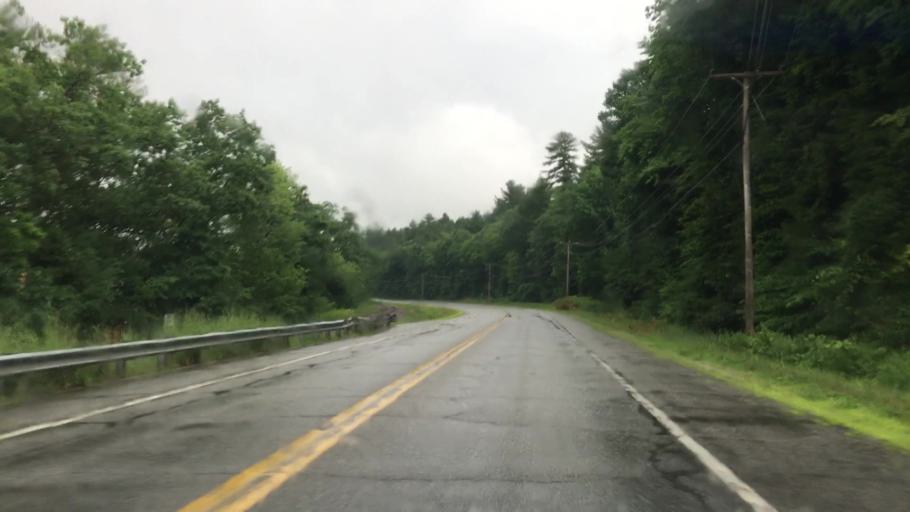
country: US
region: Maine
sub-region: Kennebec County
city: Pittston
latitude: 44.2039
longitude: -69.7650
